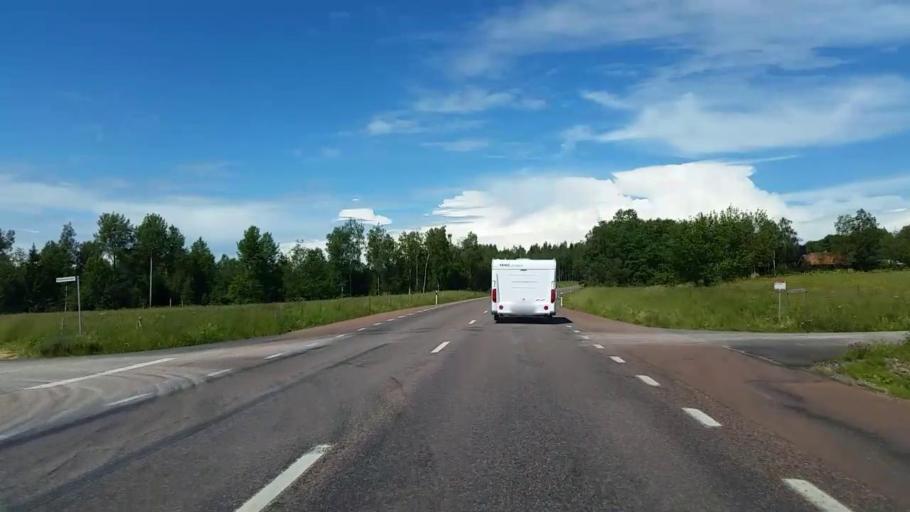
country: SE
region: Dalarna
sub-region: Rattviks Kommun
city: Raettvik
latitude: 60.9909
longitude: 15.2183
